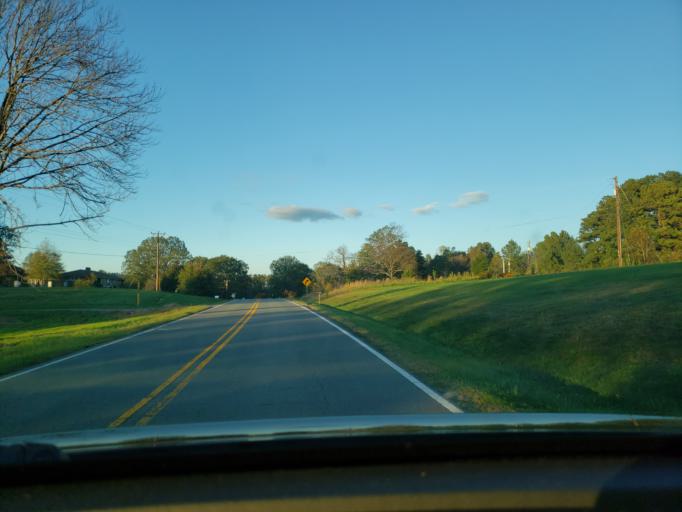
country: US
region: North Carolina
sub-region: Stokes County
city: Danbury
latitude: 36.3522
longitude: -80.2164
